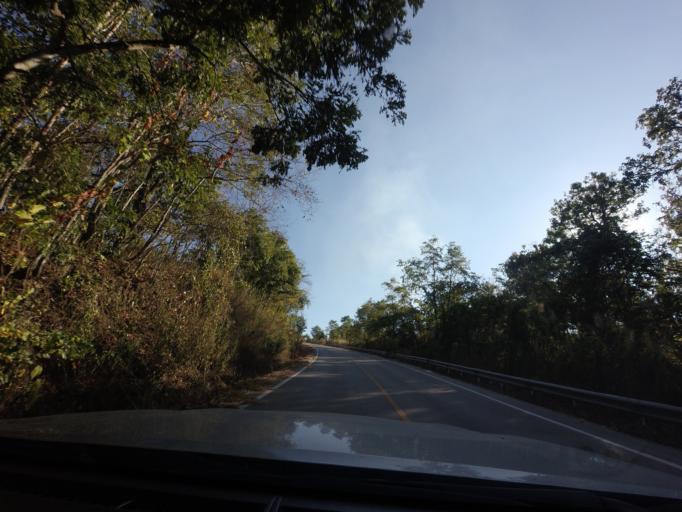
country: TH
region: Lampang
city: Chae Hom
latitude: 18.5761
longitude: 99.6270
